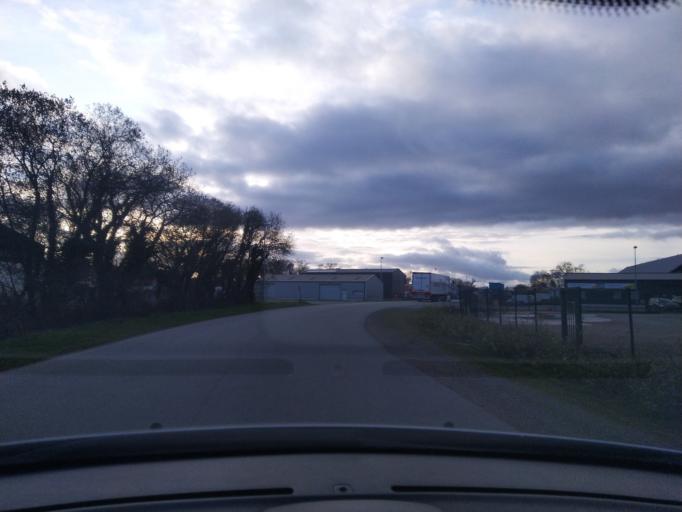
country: FR
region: Brittany
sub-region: Departement du Finistere
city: Plouigneau
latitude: 48.5730
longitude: -3.7151
